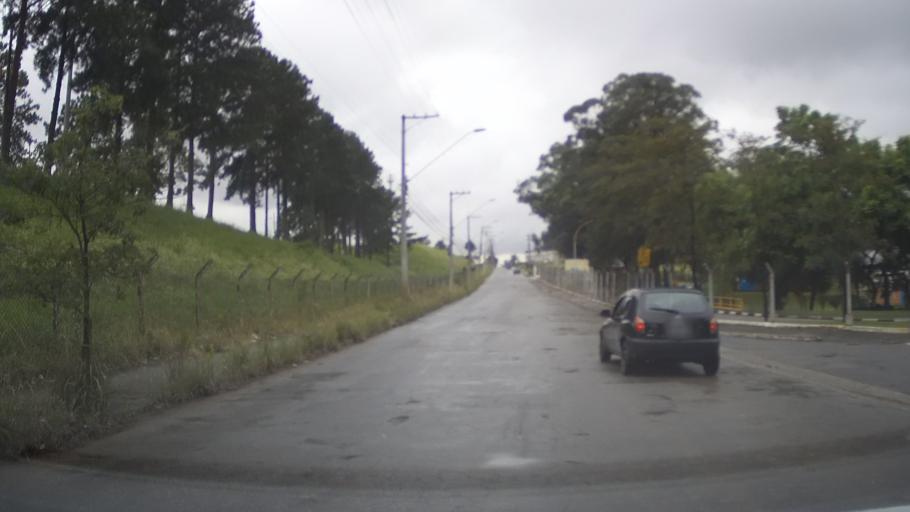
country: BR
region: Sao Paulo
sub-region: Guarulhos
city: Guarulhos
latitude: -23.4703
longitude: -46.4502
